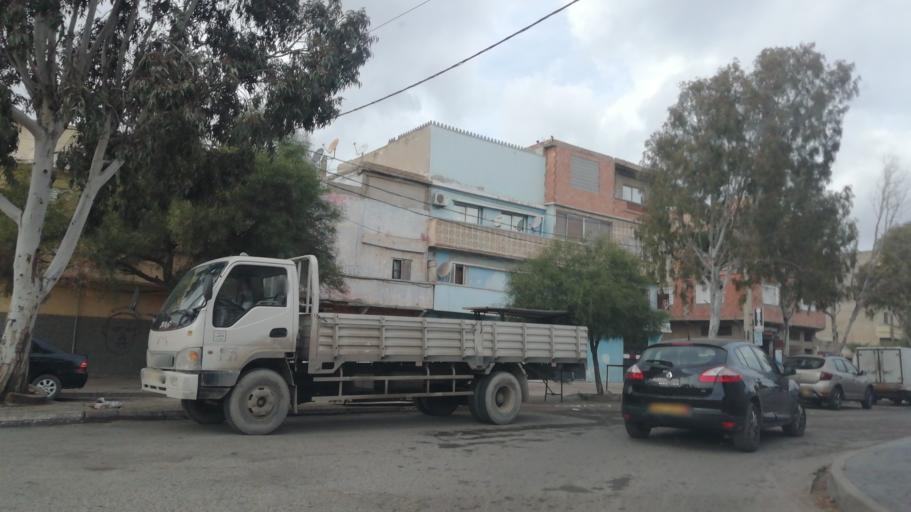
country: DZ
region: Oran
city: Oran
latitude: 35.6851
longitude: -0.6366
